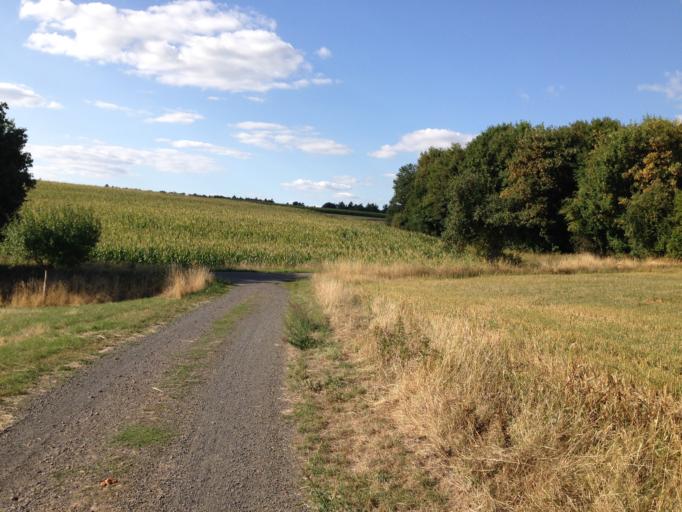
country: DE
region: Hesse
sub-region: Regierungsbezirk Giessen
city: Reiskirchen
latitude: 50.6226
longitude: 8.8631
